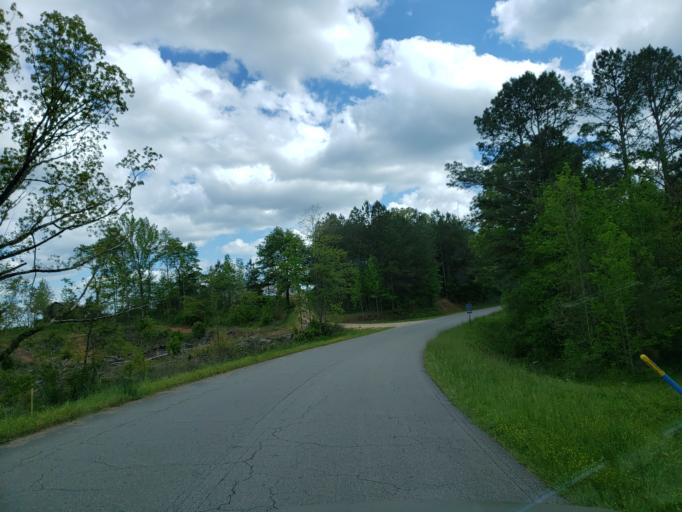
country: US
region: Georgia
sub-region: Haralson County
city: Tallapoosa
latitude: 33.7374
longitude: -85.3852
